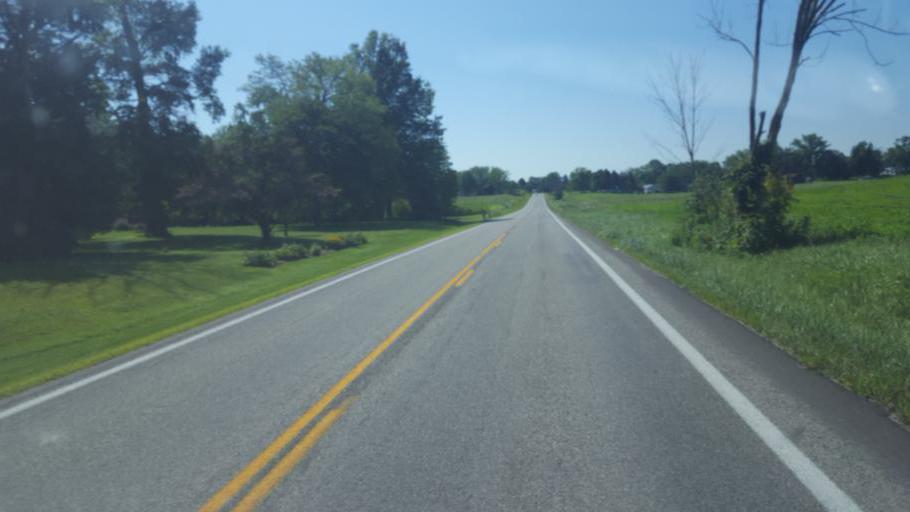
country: US
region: Ohio
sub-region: Morrow County
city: Mount Gilead
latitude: 40.5306
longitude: -82.8195
